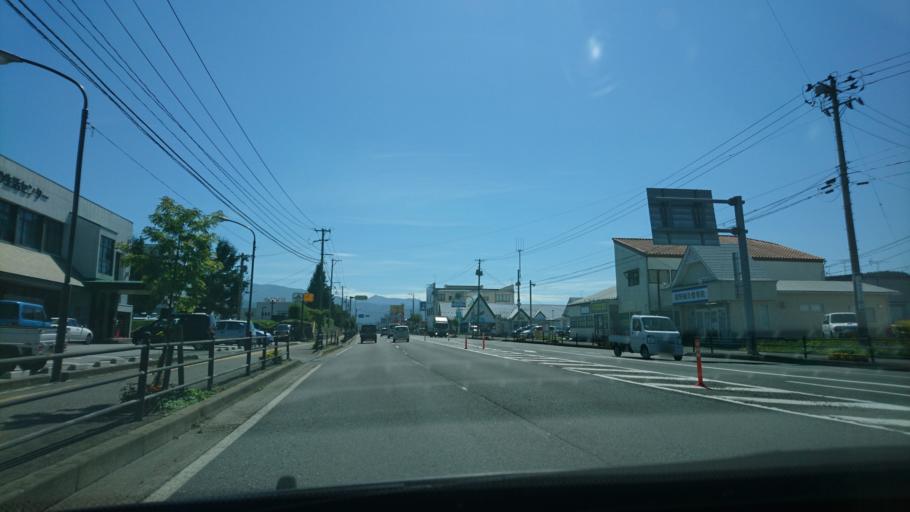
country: JP
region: Iwate
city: Tono
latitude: 39.3390
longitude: 141.5397
